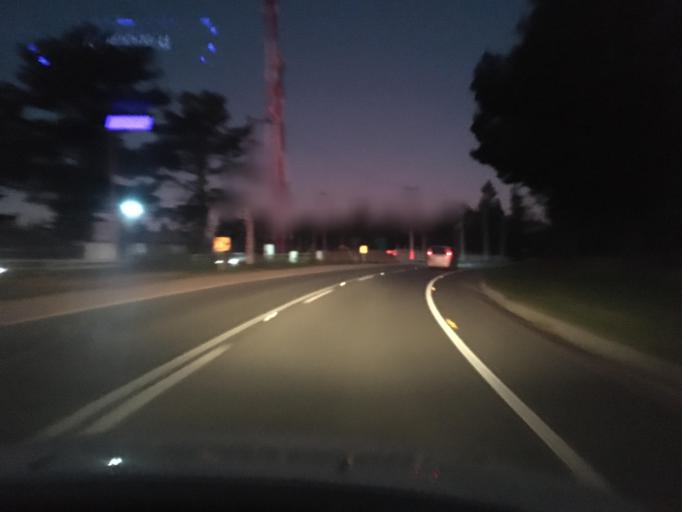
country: CL
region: Valparaiso
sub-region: San Antonio Province
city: El Tabo
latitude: -33.4247
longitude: -71.6610
